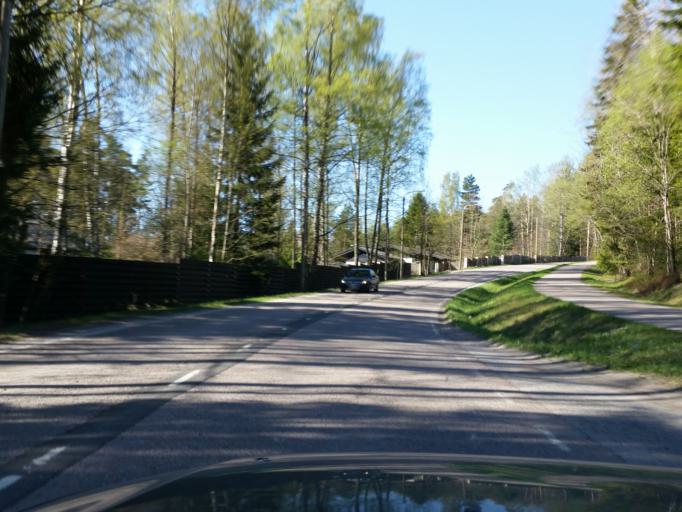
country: FI
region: Uusimaa
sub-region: Helsinki
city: Kirkkonummi
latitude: 60.1254
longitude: 24.4586
